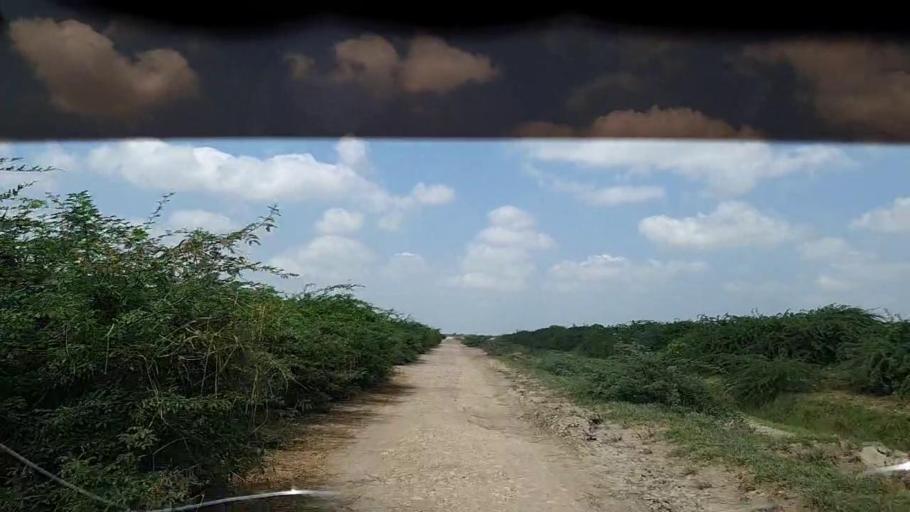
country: PK
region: Sindh
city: Kadhan
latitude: 24.5931
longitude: 68.9655
